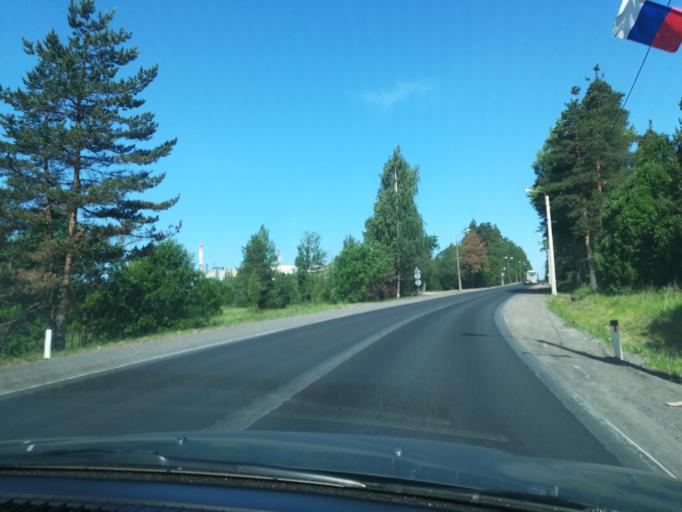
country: RU
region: Leningrad
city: Svetogorsk
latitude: 61.0987
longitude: 28.8751
